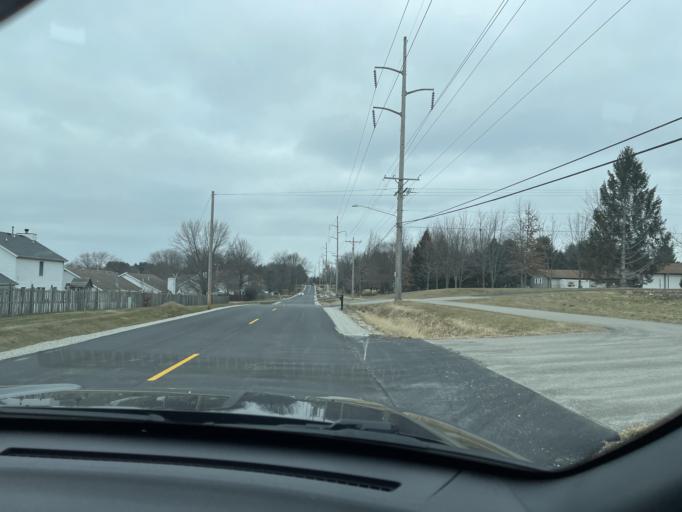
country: US
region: Illinois
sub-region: Sangamon County
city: Rochester
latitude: 39.7670
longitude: -89.5787
